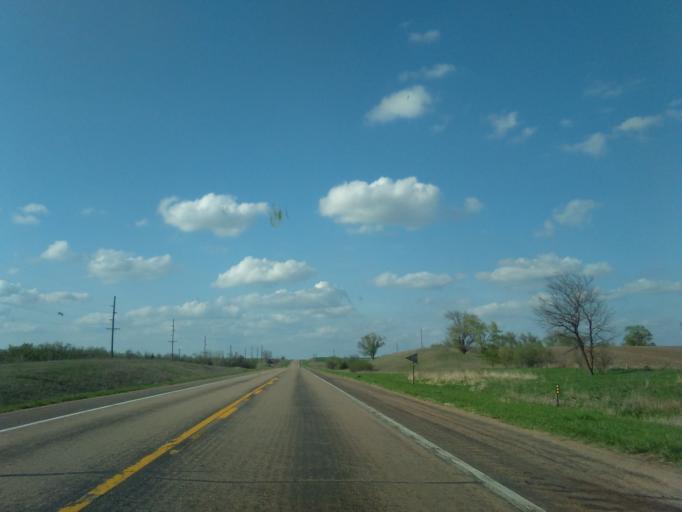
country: US
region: Nebraska
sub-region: Webster County
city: Red Cloud
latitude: 40.1107
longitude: -98.5188
